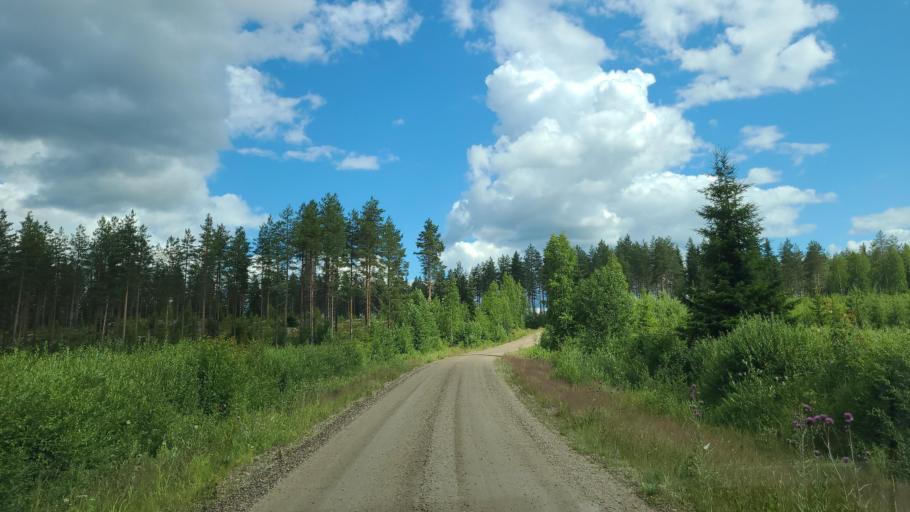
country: FI
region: Northern Savo
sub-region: Koillis-Savo
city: Kaavi
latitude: 63.0290
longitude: 28.7840
